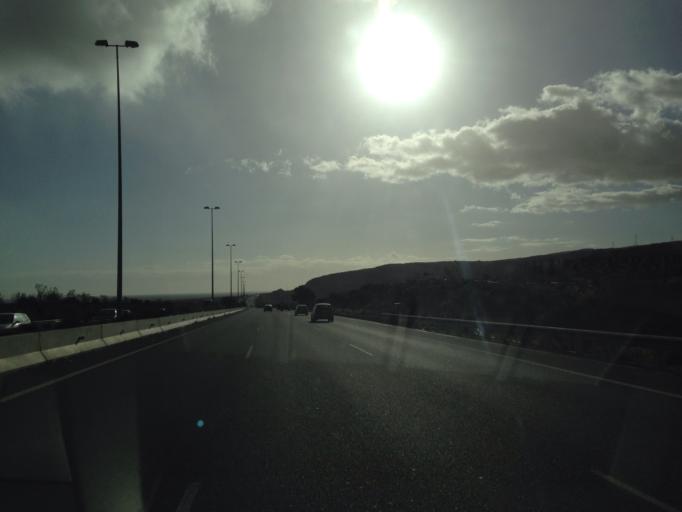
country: ES
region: Canary Islands
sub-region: Provincia de Las Palmas
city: Cruce de Arinaga
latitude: 27.8106
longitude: -15.4776
